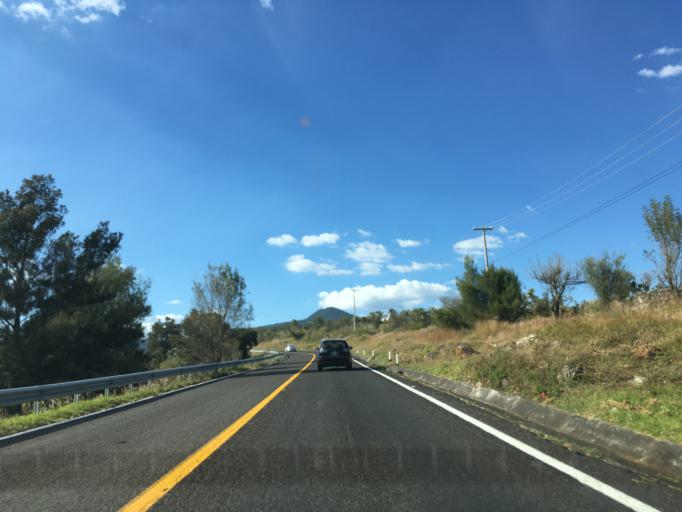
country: MX
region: Michoacan
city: Tzintzuntzan
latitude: 19.5733
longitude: -101.5744
